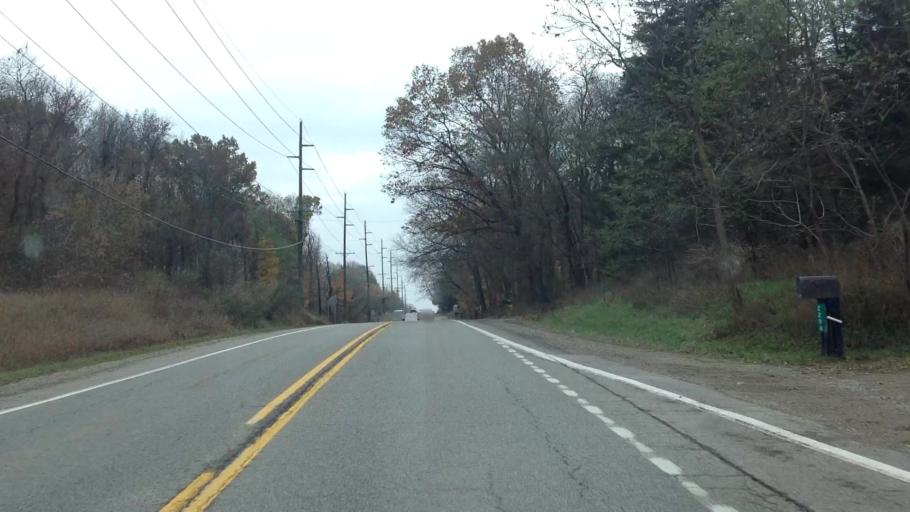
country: US
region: Michigan
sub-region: Oakland County
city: Milford
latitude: 42.6163
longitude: -83.6607
